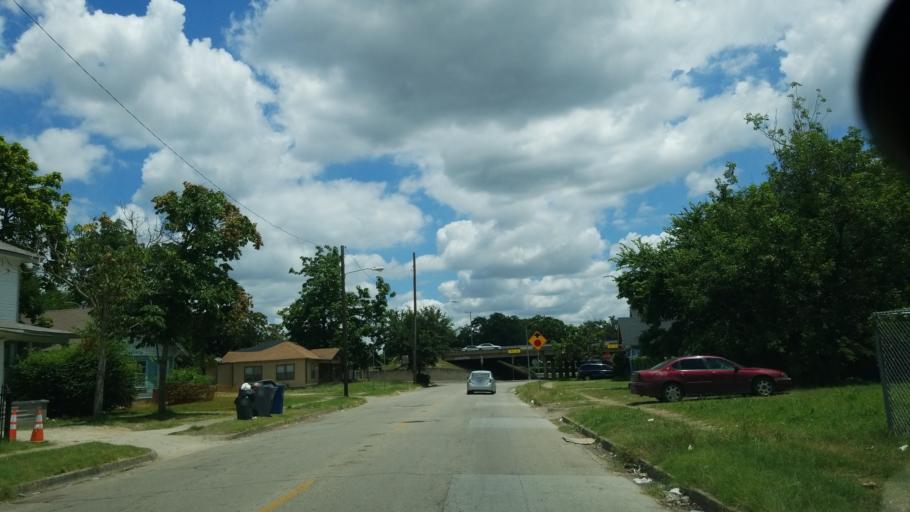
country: US
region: Texas
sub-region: Dallas County
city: Dallas
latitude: 32.7526
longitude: -96.7660
